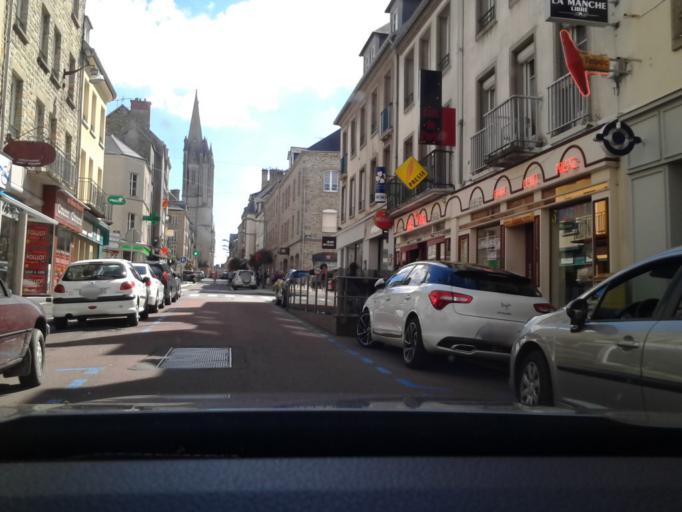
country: FR
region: Lower Normandy
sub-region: Departement de la Manche
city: Coutances
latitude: 49.0502
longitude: -1.4438
